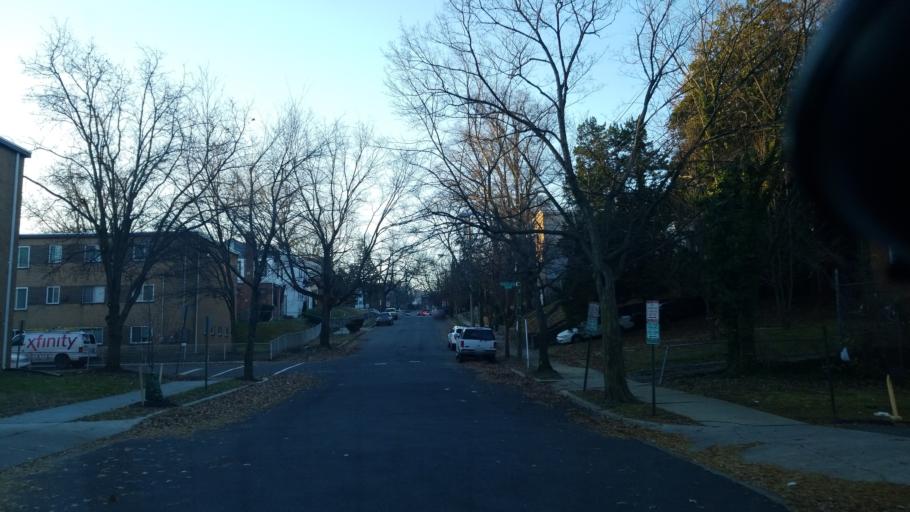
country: US
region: Maryland
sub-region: Prince George's County
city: Silver Hill
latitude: 38.8742
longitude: -76.9665
